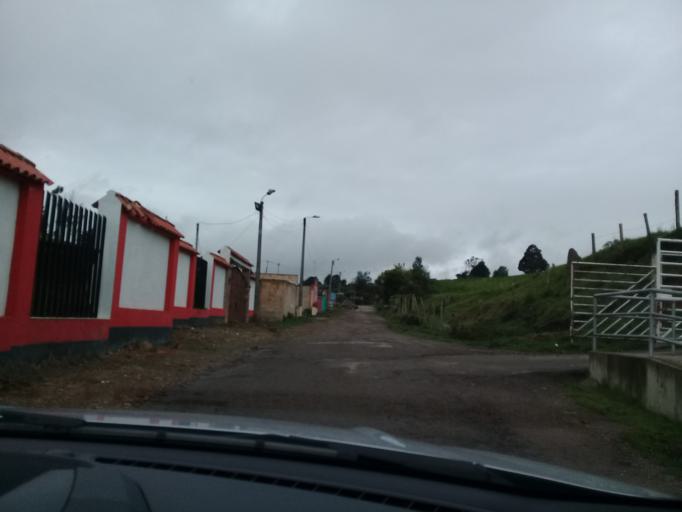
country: CO
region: Boyaca
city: Samaca
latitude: 5.4324
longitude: -73.4504
